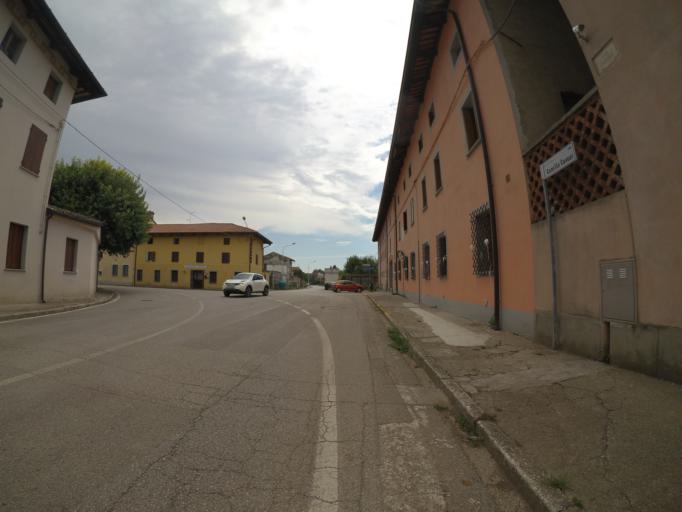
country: IT
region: Friuli Venezia Giulia
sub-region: Provincia di Udine
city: Castions di Strada
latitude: 45.9164
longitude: 13.1564
